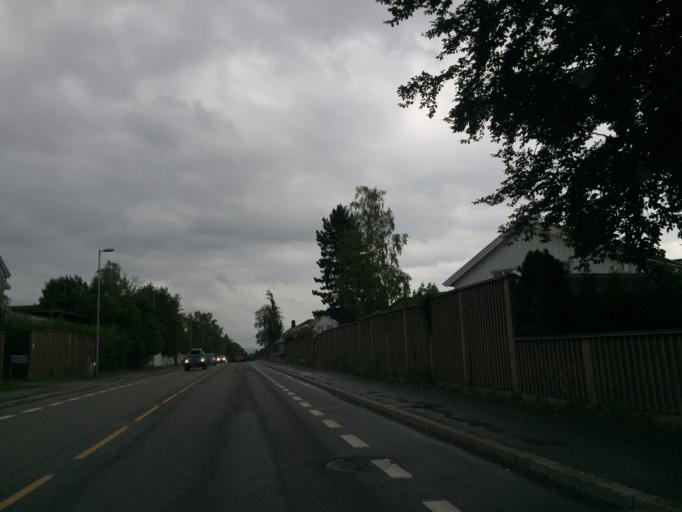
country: NO
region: Oslo
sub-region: Oslo
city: Sjolyststranda
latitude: 59.9466
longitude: 10.6772
